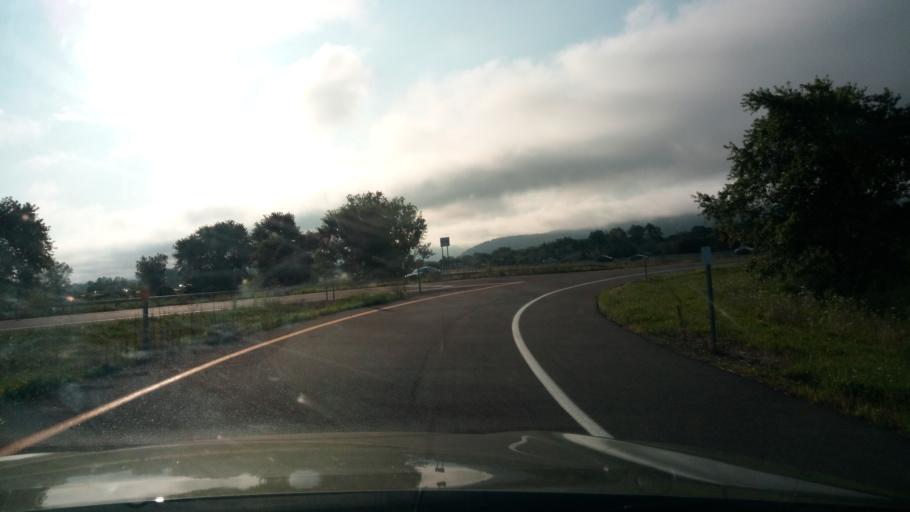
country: US
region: New York
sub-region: Chemung County
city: Big Flats
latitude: 42.1305
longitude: -76.9771
